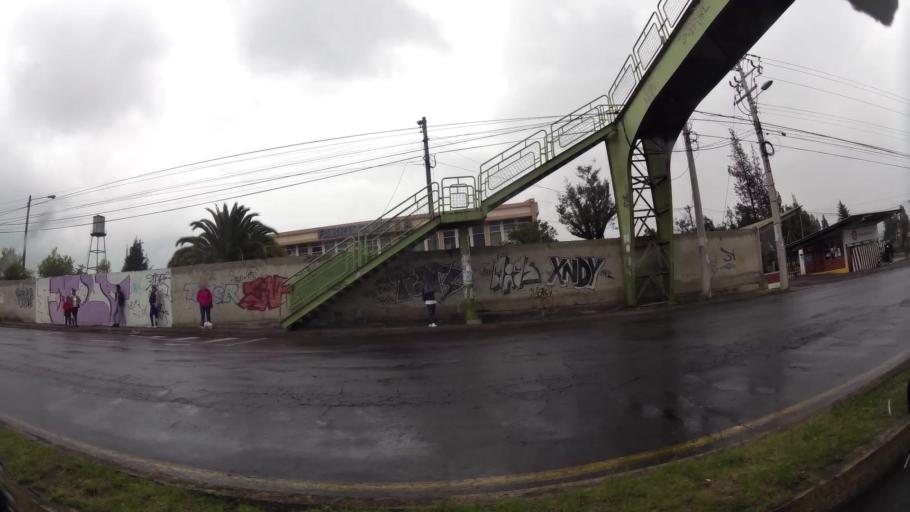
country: EC
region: Pichincha
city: Sangolqui
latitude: -0.3207
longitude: -78.4425
